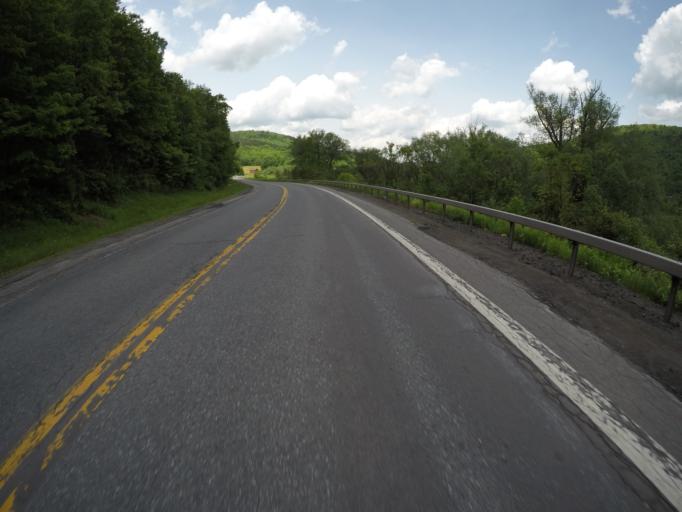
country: US
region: New York
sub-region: Delaware County
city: Stamford
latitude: 42.1555
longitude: -74.6242
